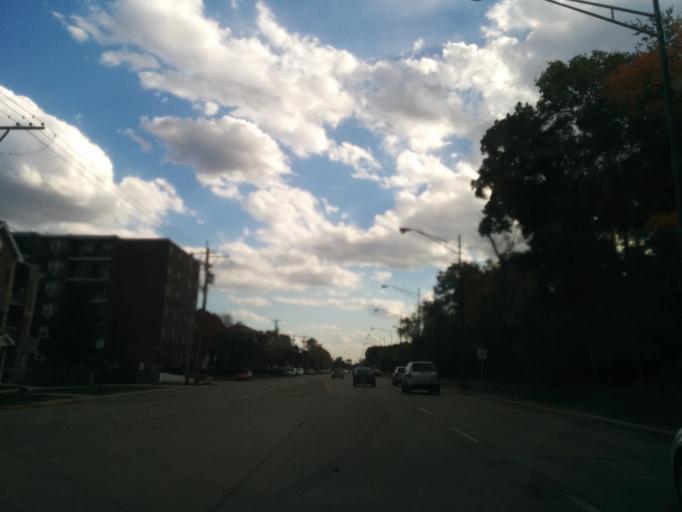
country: US
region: Illinois
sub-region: Cook County
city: Norridge
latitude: 41.9770
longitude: -87.8466
